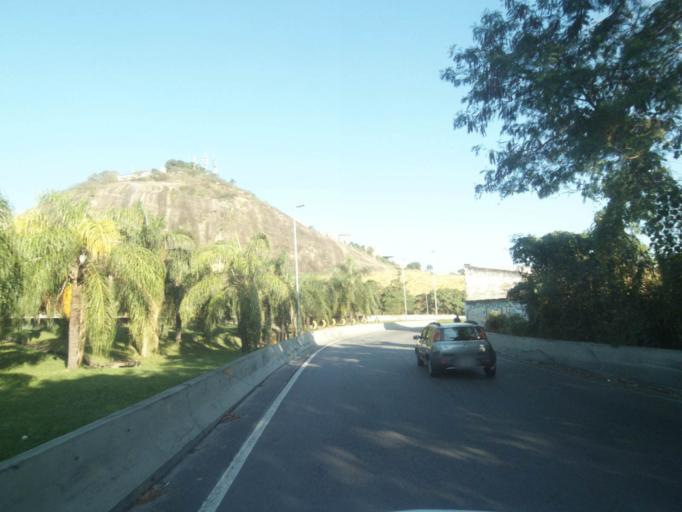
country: BR
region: Rio de Janeiro
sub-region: Sao Joao De Meriti
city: Sao Joao de Meriti
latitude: -22.9392
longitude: -43.3508
